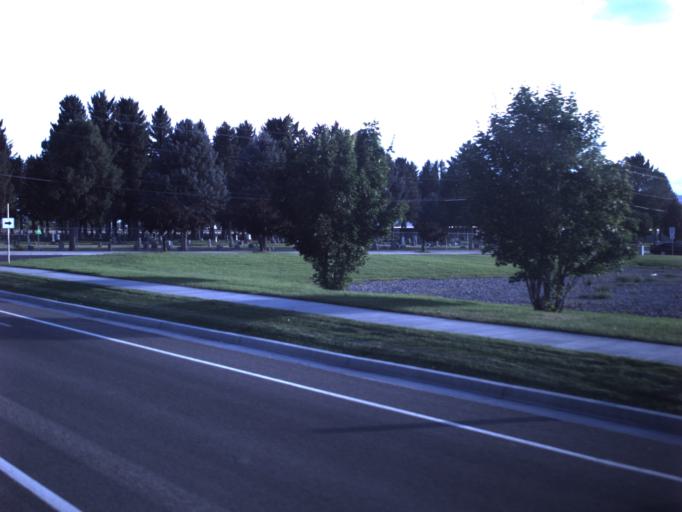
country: US
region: Utah
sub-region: Sanpete County
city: Ephraim
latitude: 39.3734
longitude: -111.5871
